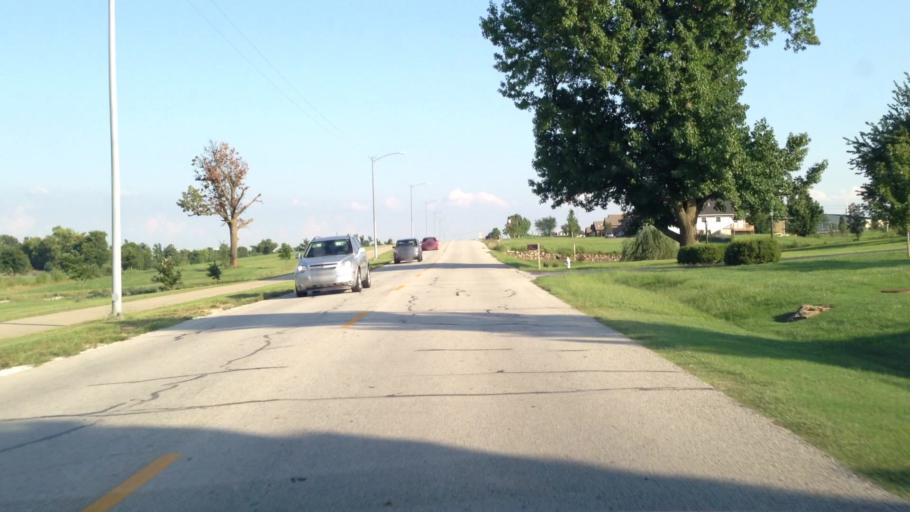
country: US
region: Missouri
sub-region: Jasper County
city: Joplin
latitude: 37.0736
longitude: -94.4897
